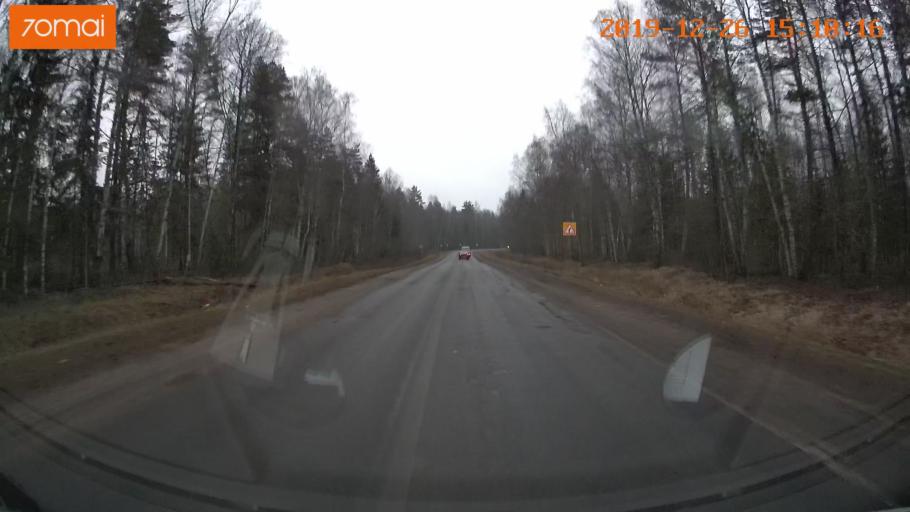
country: RU
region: Jaroslavl
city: Rybinsk
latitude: 58.1416
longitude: 38.8497
